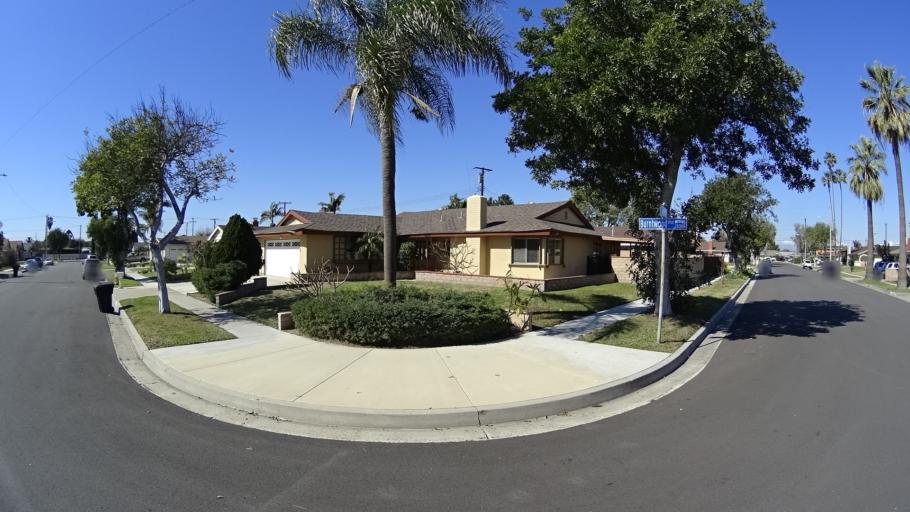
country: US
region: California
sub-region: Orange County
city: Placentia
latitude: 33.8295
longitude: -117.8700
